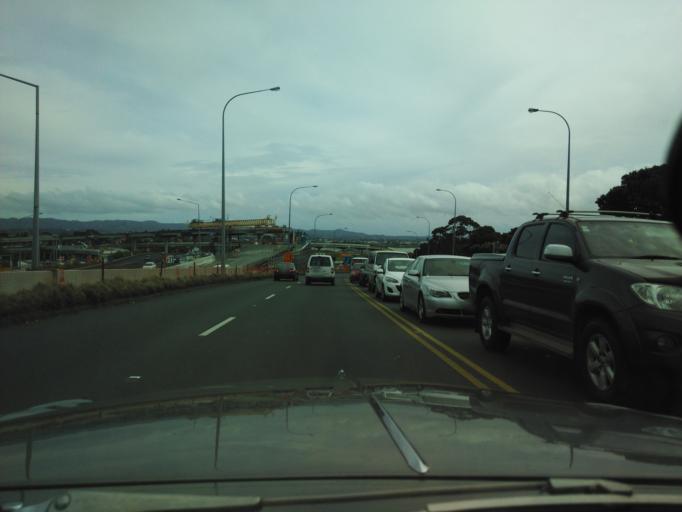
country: NZ
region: Auckland
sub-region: Auckland
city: Rosebank
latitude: -36.8712
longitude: 174.7088
